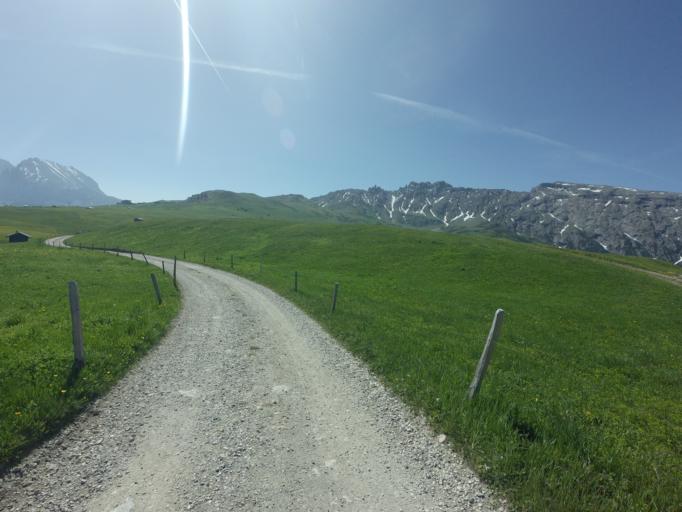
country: IT
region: Trentino-Alto Adige
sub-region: Bolzano
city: Siusi
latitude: 46.5256
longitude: 11.6220
